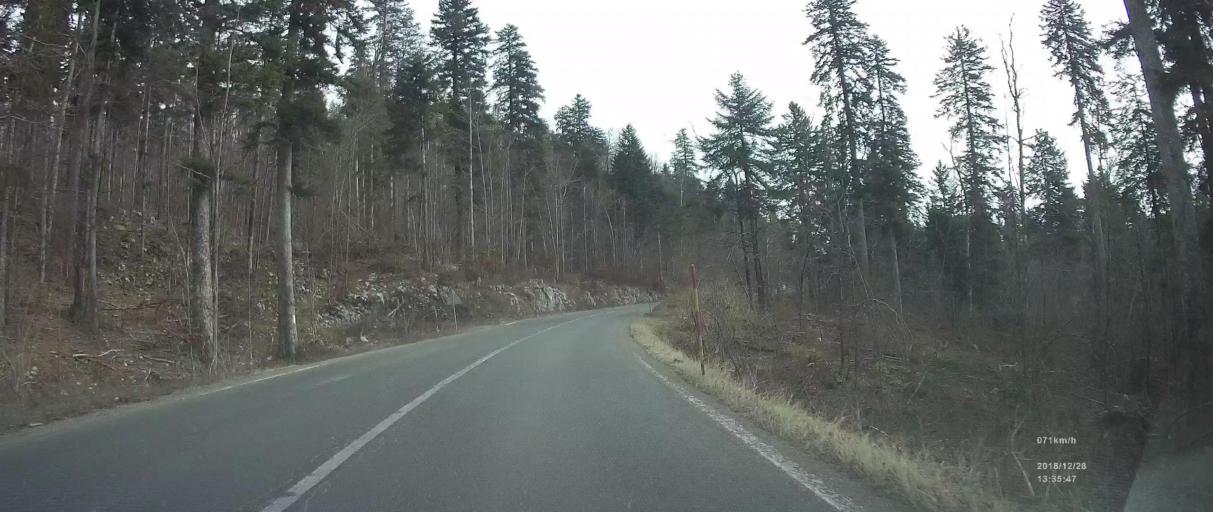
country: HR
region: Primorsko-Goranska
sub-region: Grad Delnice
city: Delnice
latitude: 45.3510
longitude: 14.6958
